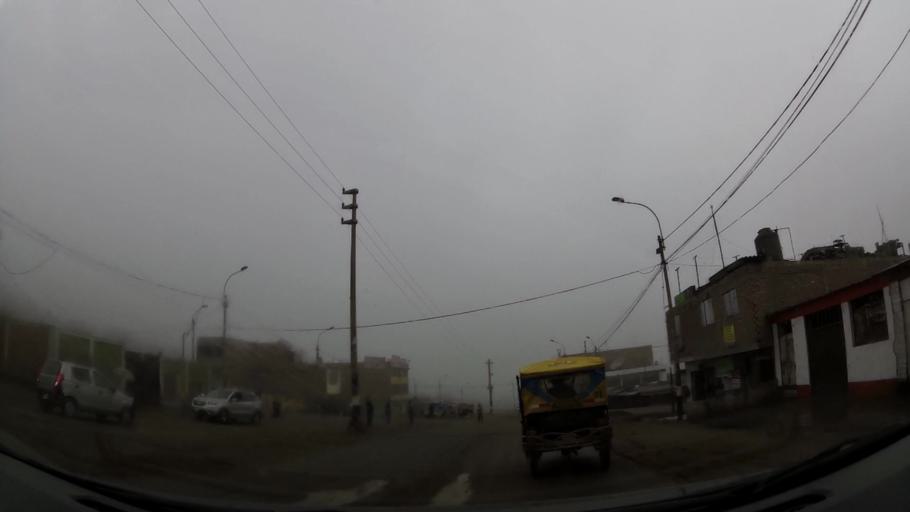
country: PE
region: Lima
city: Ventanilla
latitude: -11.8343
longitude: -77.1380
